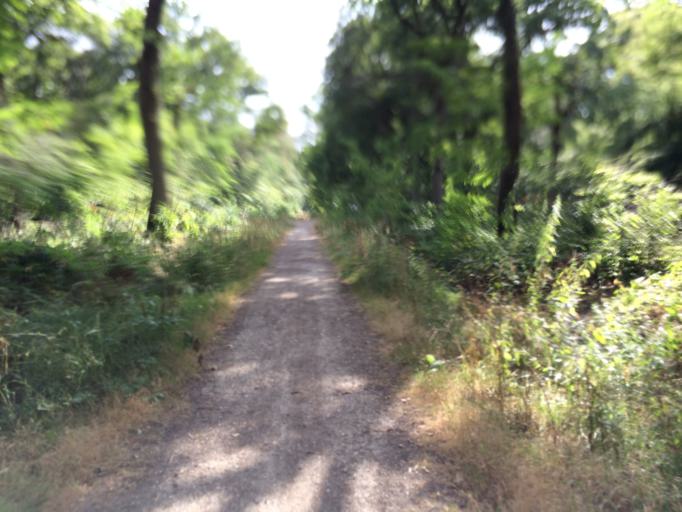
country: FR
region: Ile-de-France
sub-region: Departement de l'Essonne
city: Quincy-sous-Senart
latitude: 48.6717
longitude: 2.5229
